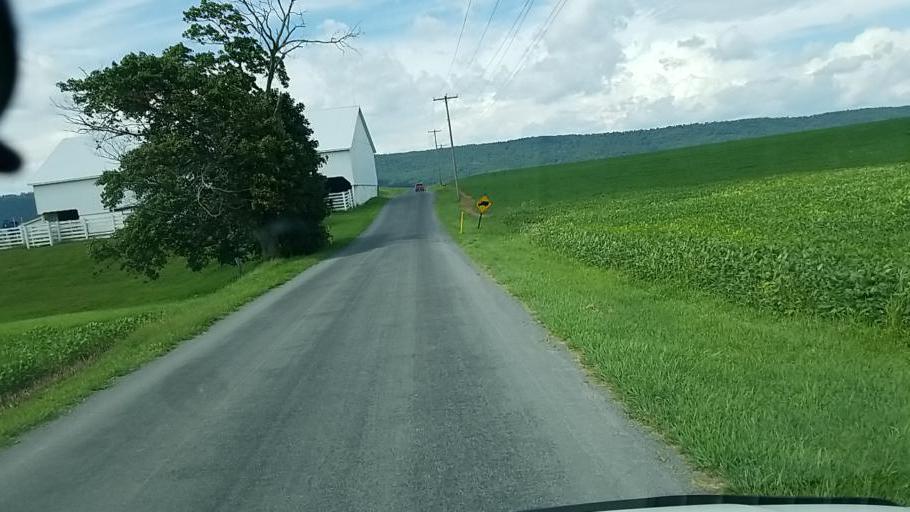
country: US
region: Pennsylvania
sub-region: Dauphin County
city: Elizabethville
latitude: 40.5892
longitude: -76.8456
